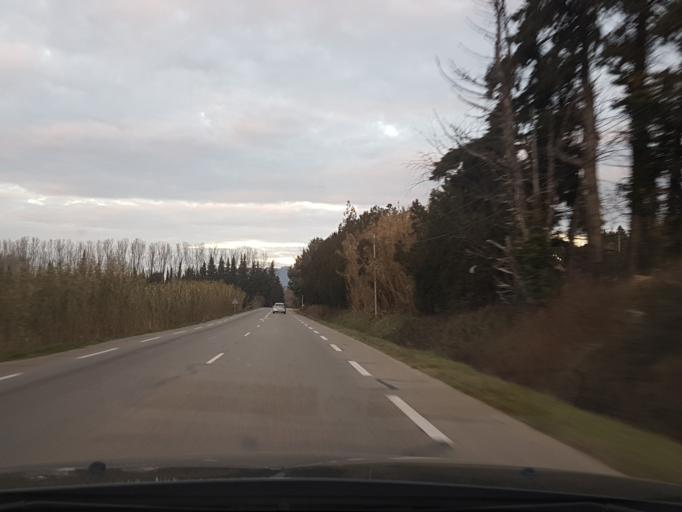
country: FR
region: Provence-Alpes-Cote d'Azur
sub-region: Departement du Vaucluse
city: Loriol-du-Comtat
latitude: 44.0650
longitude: 5.0023
